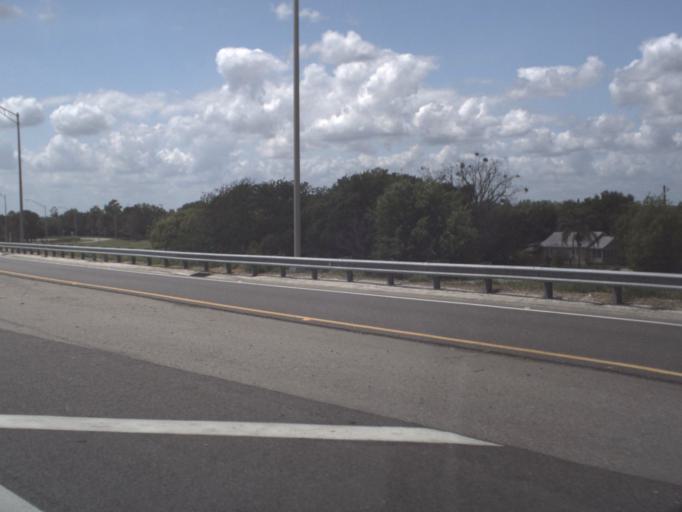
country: US
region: Florida
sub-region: Orange County
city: Ocoee
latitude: 28.5777
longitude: -81.5573
